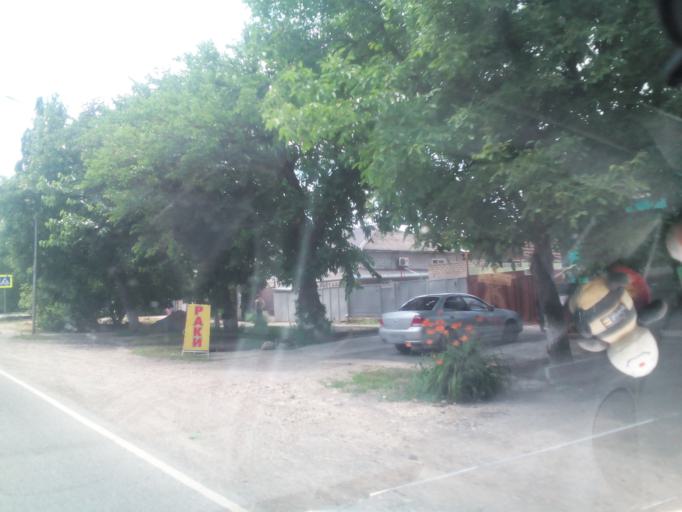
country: RU
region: Stavropol'skiy
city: Inozemtsevo
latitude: 44.1055
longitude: 43.0923
